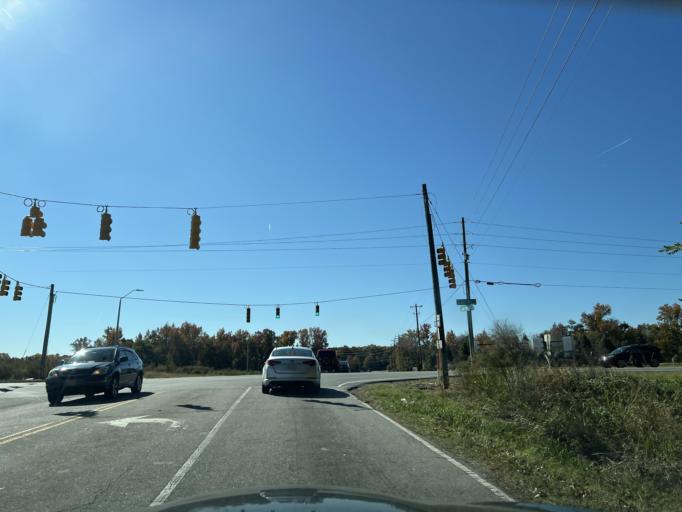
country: US
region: North Carolina
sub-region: Wake County
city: Garner
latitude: 35.6712
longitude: -78.7062
